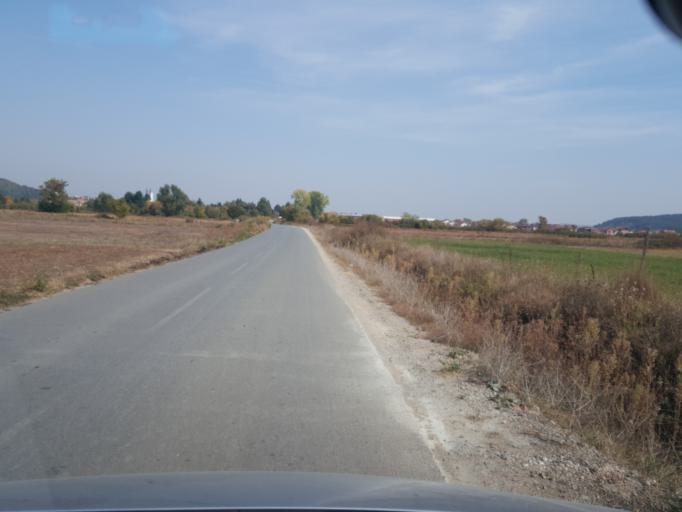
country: XK
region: Gjakova
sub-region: Komuna e Gjakoves
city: Gjakove
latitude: 42.3698
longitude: 20.4016
